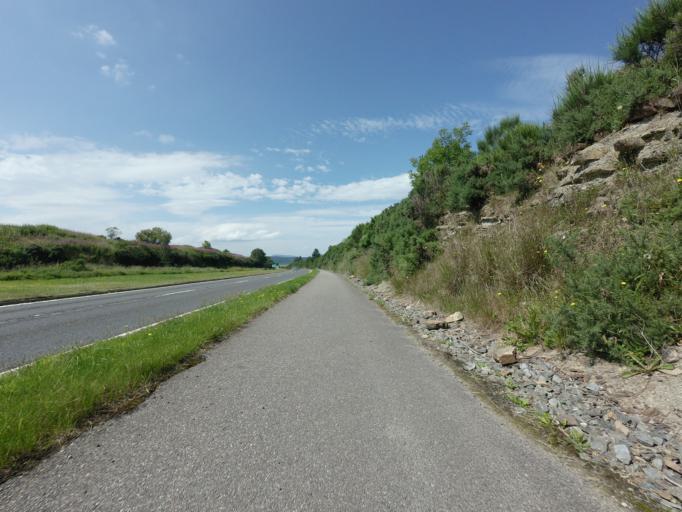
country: GB
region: Scotland
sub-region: Highland
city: Conon Bridge
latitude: 57.5501
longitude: -4.3964
